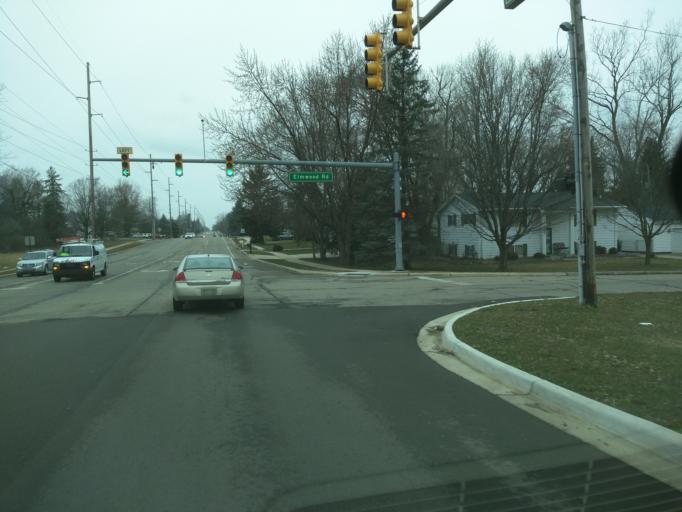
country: US
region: Michigan
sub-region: Eaton County
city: Waverly
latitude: 42.7555
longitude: -84.6223
